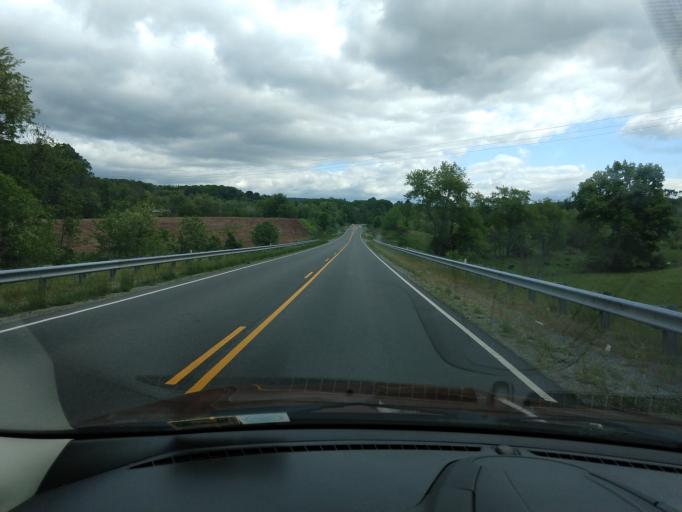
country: US
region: Virginia
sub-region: Wythe County
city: Wytheville
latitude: 36.8868
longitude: -80.9773
